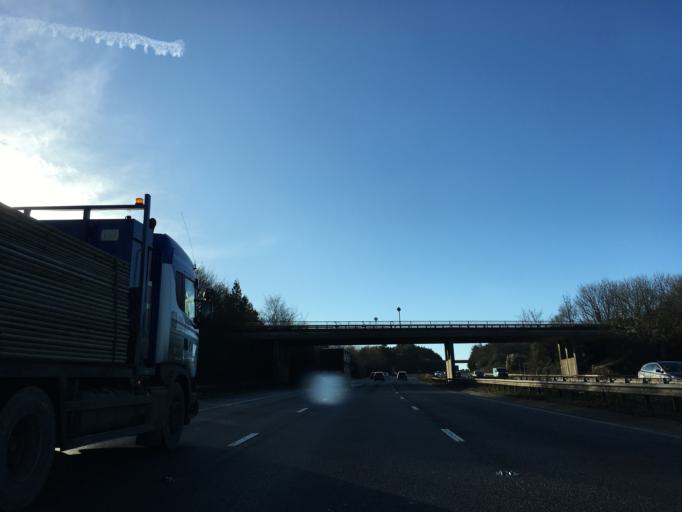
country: GB
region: England
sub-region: South Gloucestershire
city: Tytherington
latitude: 51.6085
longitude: -2.4682
